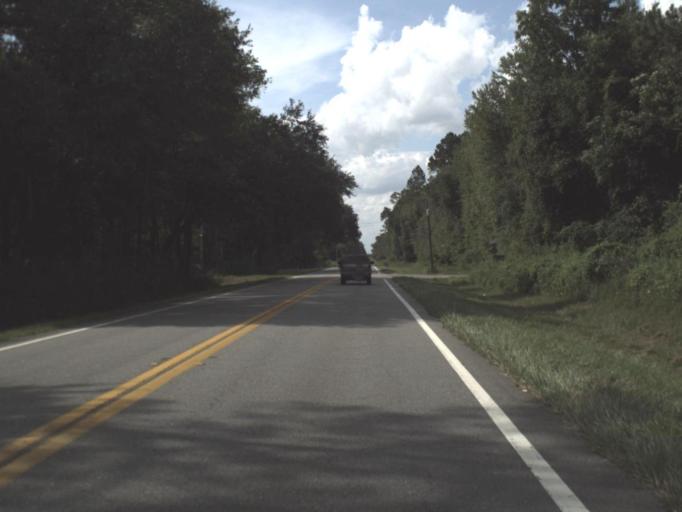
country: US
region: Florida
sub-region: Taylor County
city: Perry
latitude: 30.3437
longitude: -83.6475
